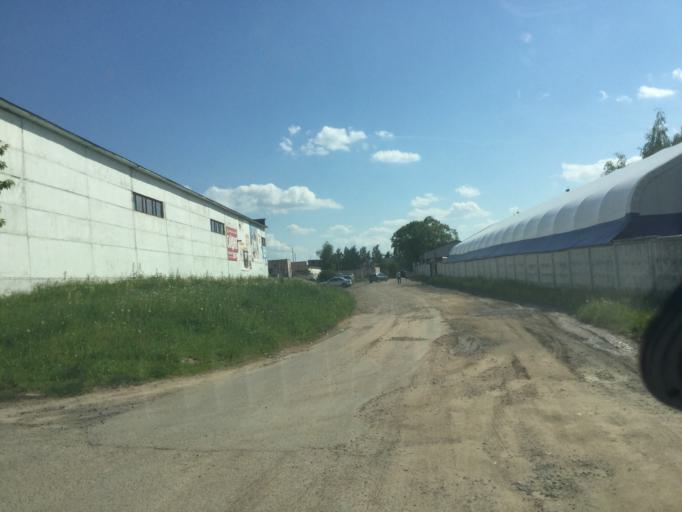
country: BY
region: Vitebsk
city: Vitebsk
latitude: 55.1665
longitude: 30.2429
